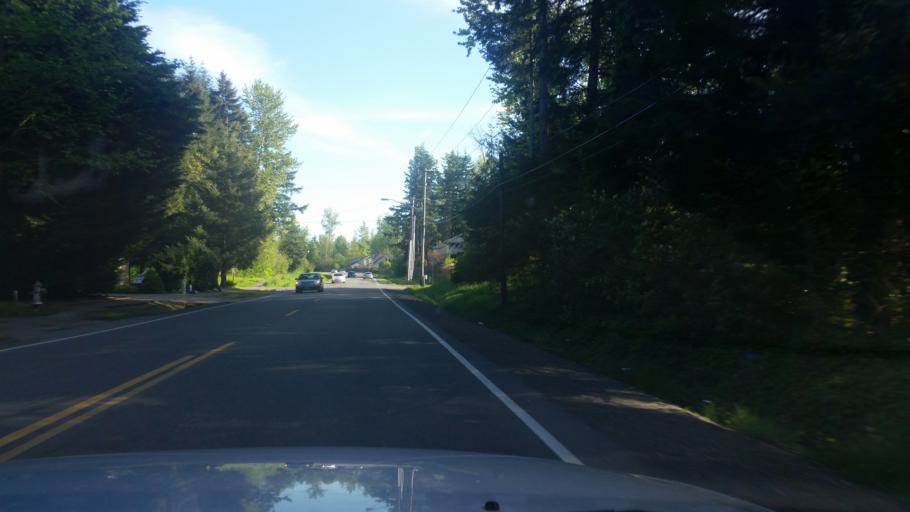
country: US
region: Washington
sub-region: Pierce County
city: South Hill
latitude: 47.1045
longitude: -122.2669
